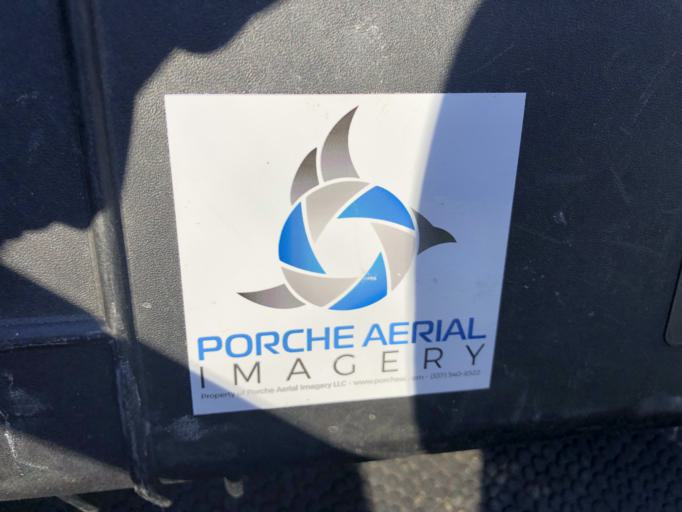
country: US
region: Louisiana
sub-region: Calcasieu Parish
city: Iowa
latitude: 30.3098
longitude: -93.0715
